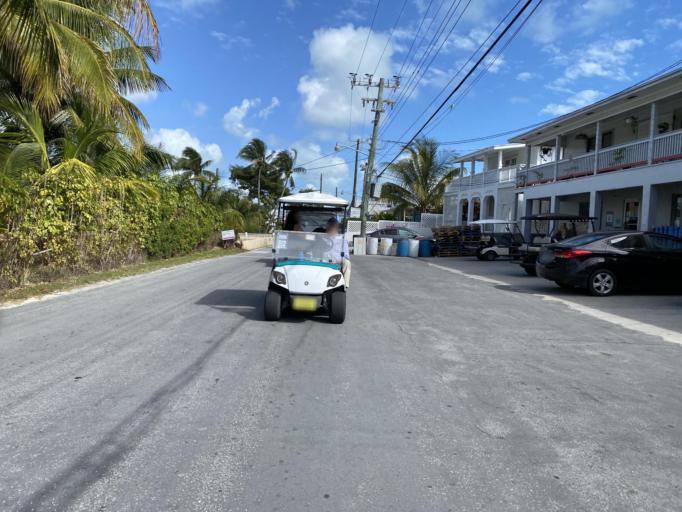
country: BS
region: Spanish Wells
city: Spanish Wells
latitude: 25.5439
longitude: -76.7515
